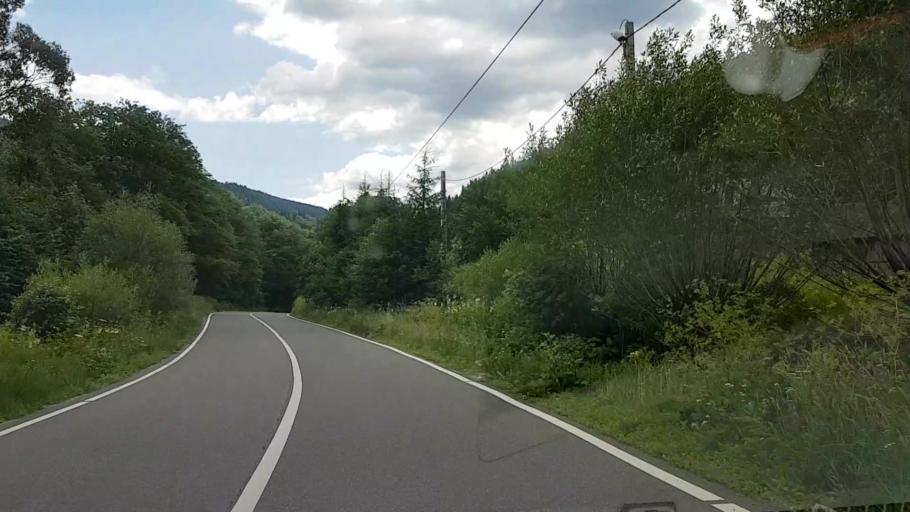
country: RO
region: Suceava
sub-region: Comuna Crucea
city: Crucea
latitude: 47.3285
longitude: 25.6202
